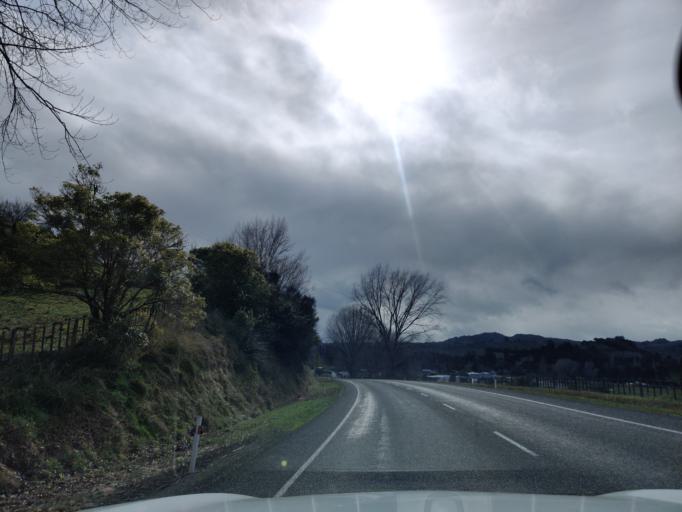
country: NZ
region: Manawatu-Wanganui
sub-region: Ruapehu District
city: Waiouru
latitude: -39.7399
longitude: 175.8396
